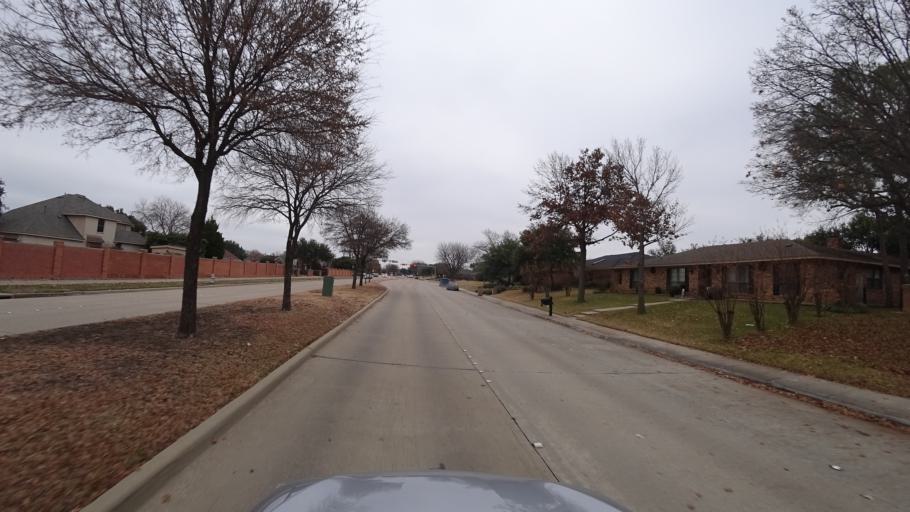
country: US
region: Texas
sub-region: Denton County
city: Lewisville
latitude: 33.0528
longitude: -97.0263
